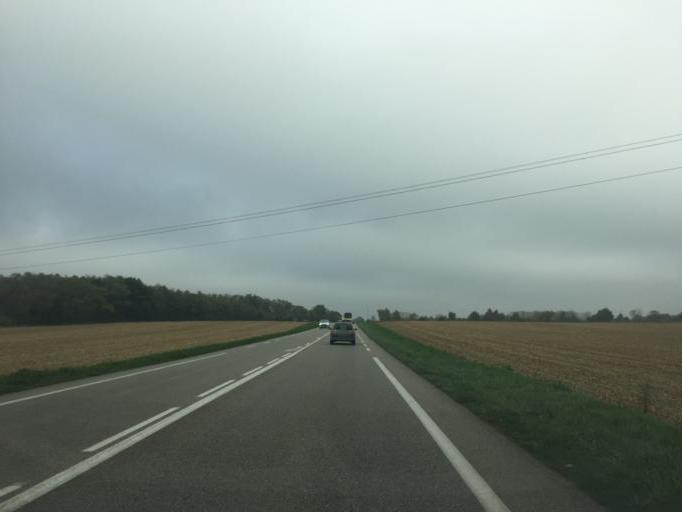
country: FR
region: Rhone-Alpes
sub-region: Departement de l'Ain
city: Saint-Andre-de-Corcy
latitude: 45.9398
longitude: 4.9701
